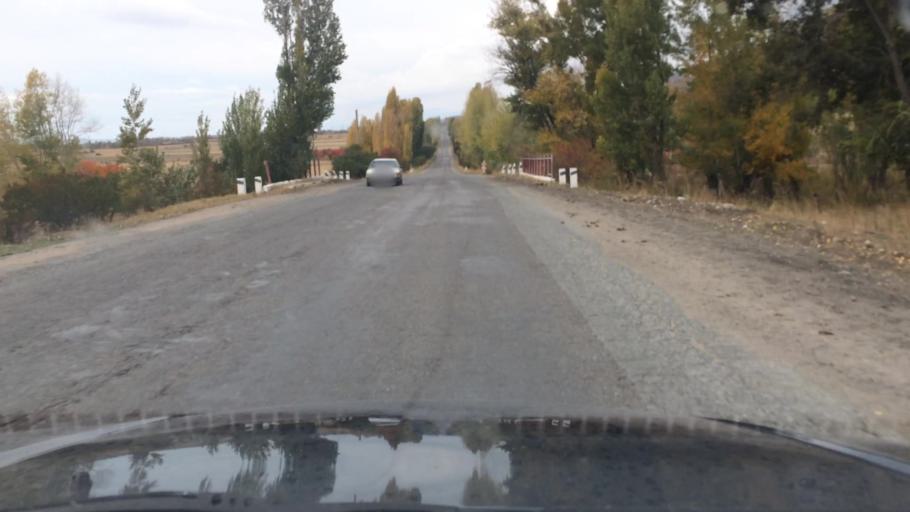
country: KG
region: Ysyk-Koel
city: Tyup
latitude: 42.7356
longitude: 77.9700
